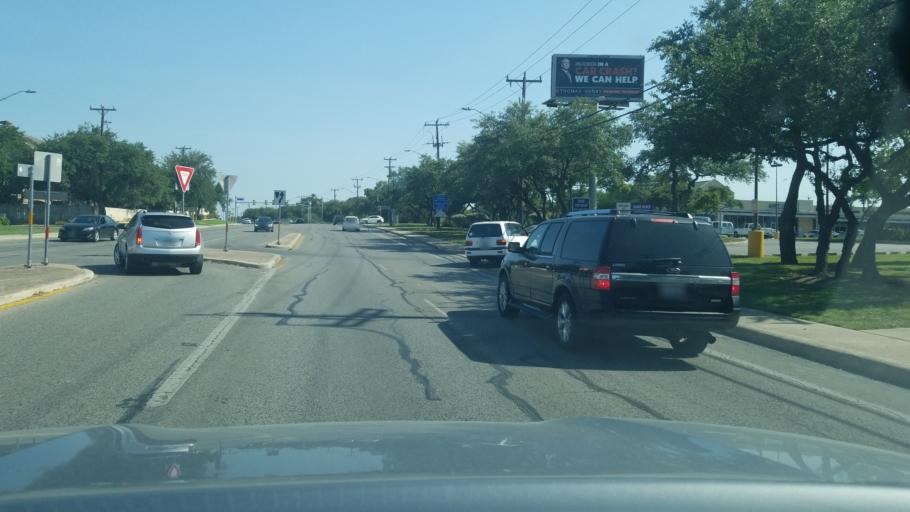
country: US
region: Texas
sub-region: Bexar County
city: Hollywood Park
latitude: 29.6071
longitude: -98.5084
